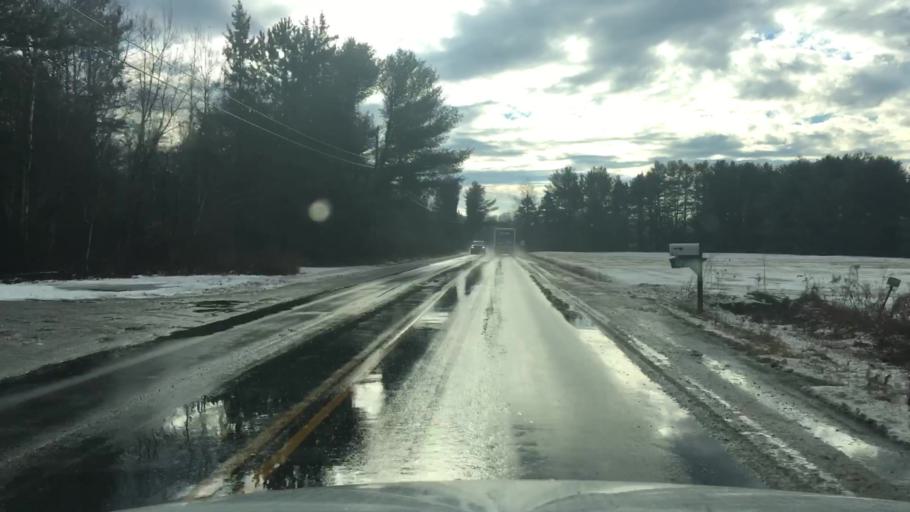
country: US
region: Maine
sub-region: Penobscot County
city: Brewer
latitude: 44.7447
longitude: -68.7661
